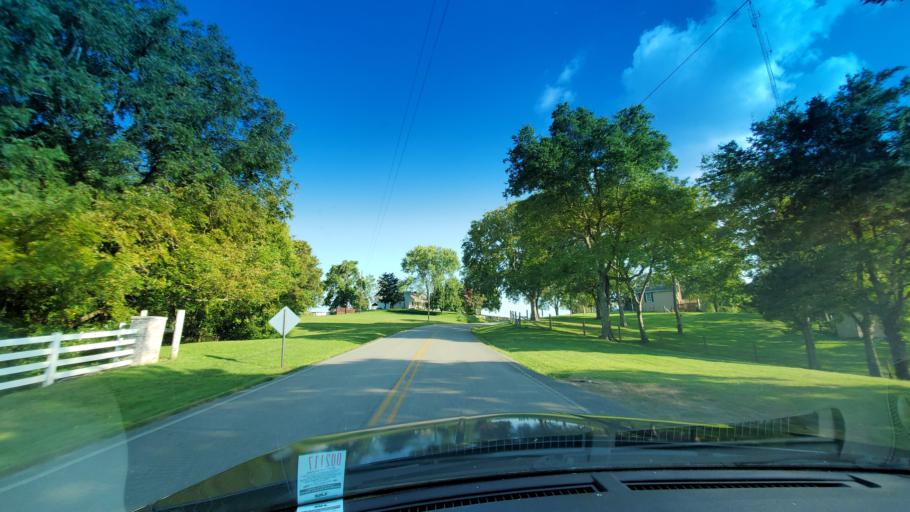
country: US
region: Tennessee
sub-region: Wilson County
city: Lebanon
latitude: 36.1598
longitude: -86.3741
